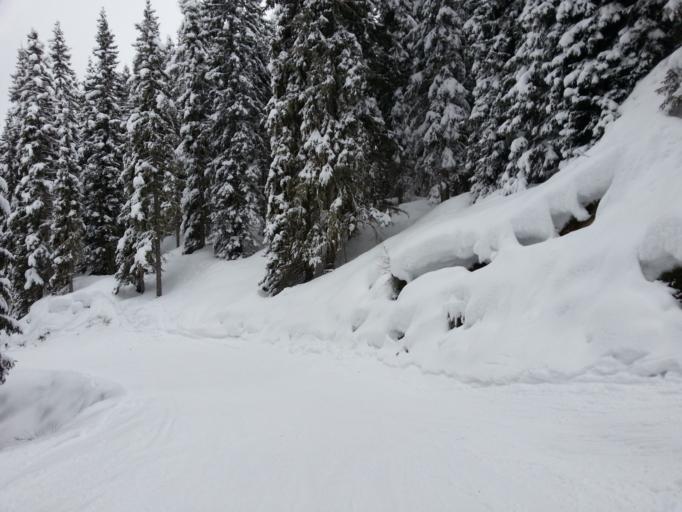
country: AT
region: Salzburg
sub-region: Politischer Bezirk Sankt Johann im Pongau
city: Flachau
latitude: 47.3030
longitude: 13.3686
